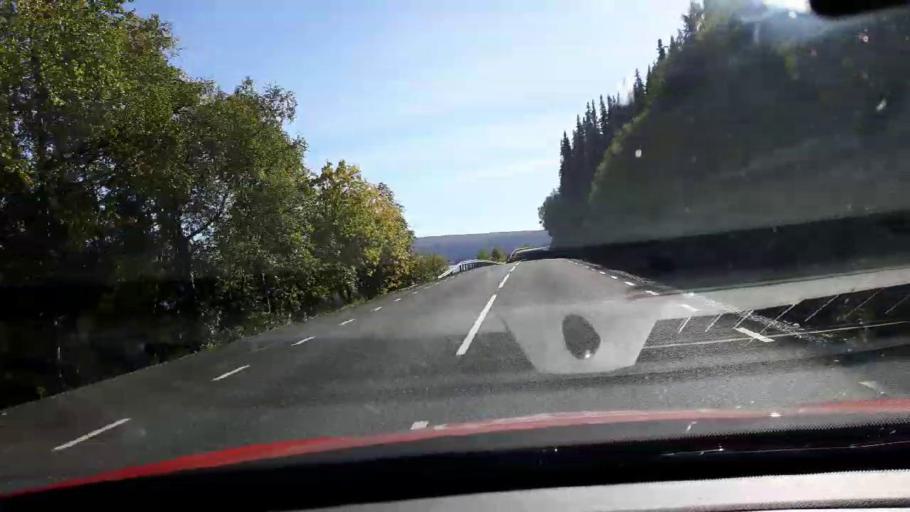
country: NO
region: Nord-Trondelag
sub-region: Royrvik
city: Royrvik
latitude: 64.8287
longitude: 14.0792
